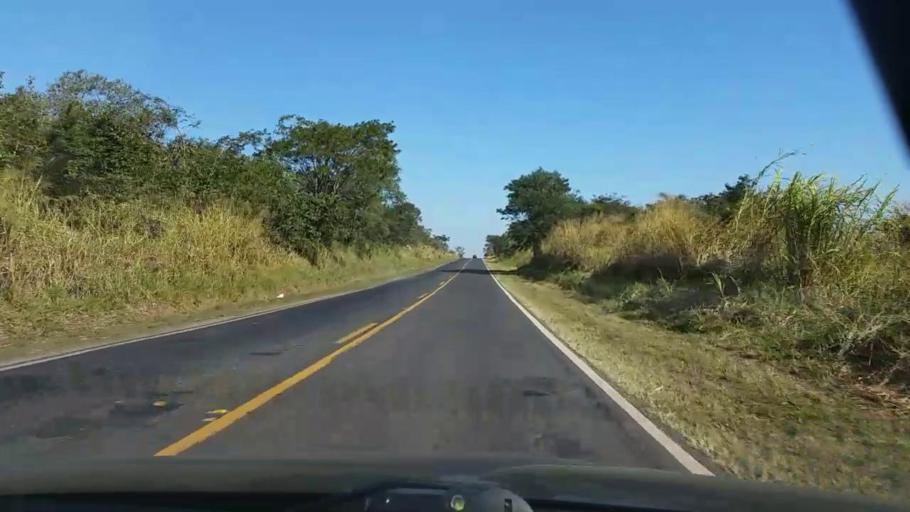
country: BR
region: Sao Paulo
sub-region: Itatinga
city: Itatinga
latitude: -22.8988
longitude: -48.7650
